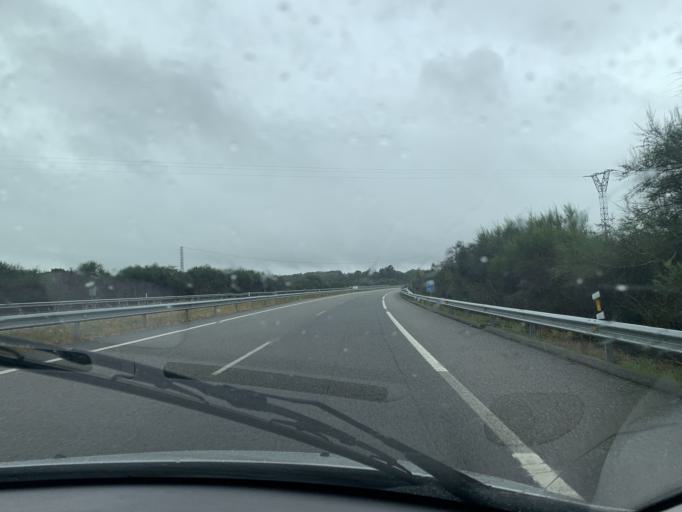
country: ES
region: Galicia
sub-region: Provincia de Lugo
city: Vilalba
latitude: 43.3297
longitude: -7.5861
